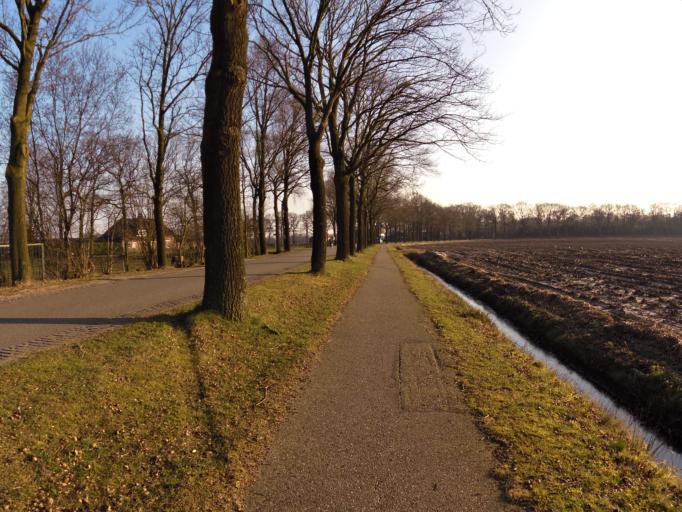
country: NL
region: North Brabant
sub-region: Gemeente Sint-Michielsgestel
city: Sint-Michielsgestel
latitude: 51.6997
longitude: 5.3858
